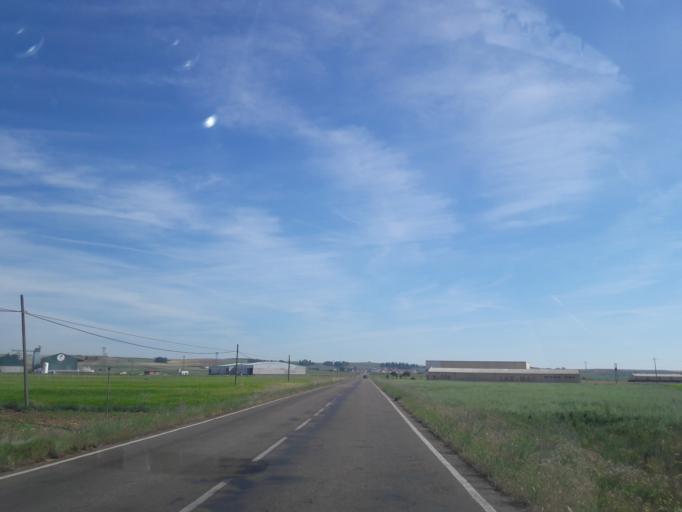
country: ES
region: Castille and Leon
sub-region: Provincia de Salamanca
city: Babilafuente
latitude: 40.9849
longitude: -5.4077
